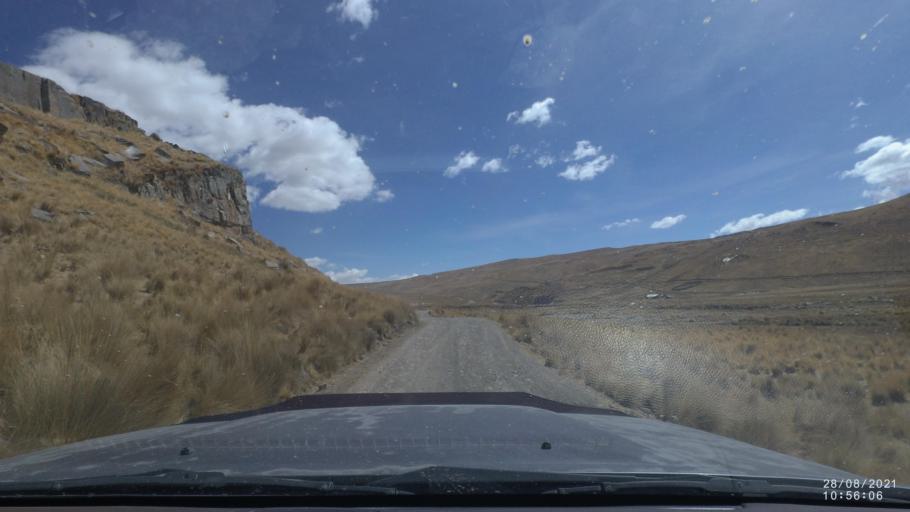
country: BO
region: Cochabamba
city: Cochabamba
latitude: -17.1952
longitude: -66.2490
